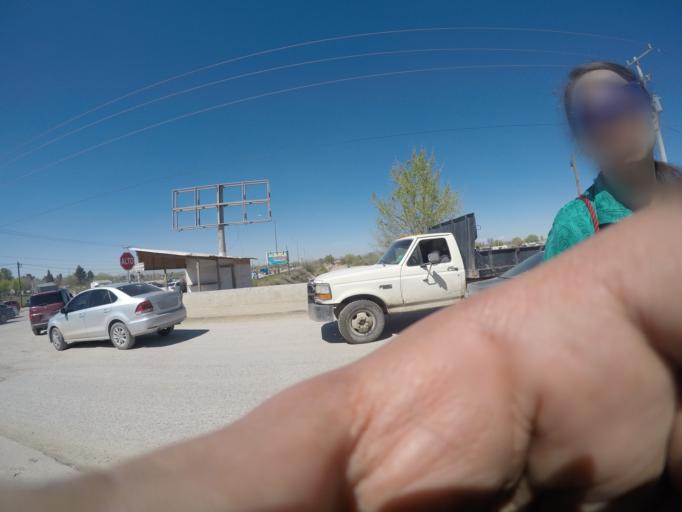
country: US
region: Texas
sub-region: El Paso County
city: Socorro Mission Number 1 Colonia
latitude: 31.6177
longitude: -106.3200
